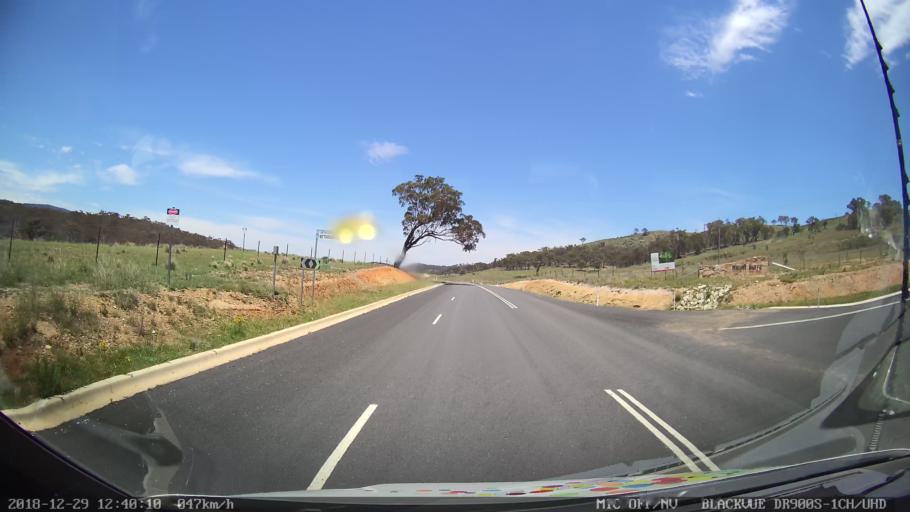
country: AU
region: Australian Capital Territory
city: Macarthur
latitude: -35.5994
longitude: 149.2258
